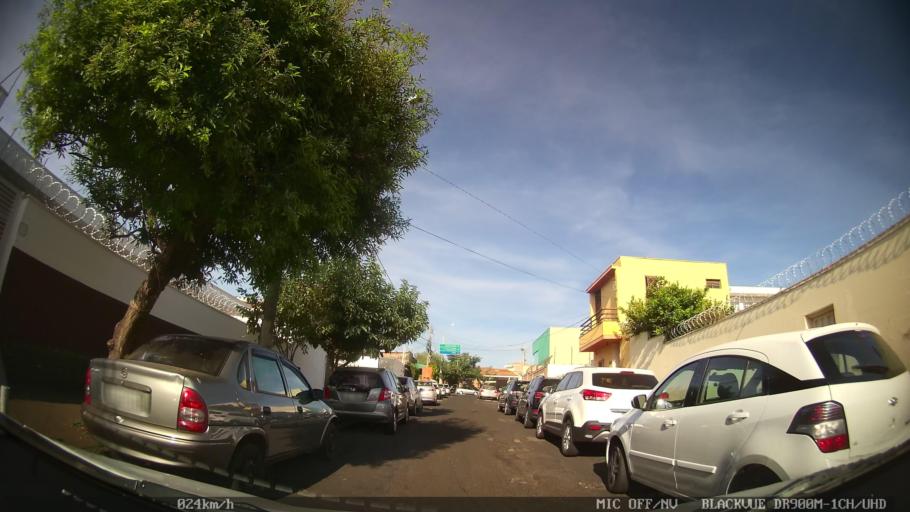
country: BR
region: Sao Paulo
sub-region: Ribeirao Preto
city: Ribeirao Preto
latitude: -21.1906
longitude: -47.8056
